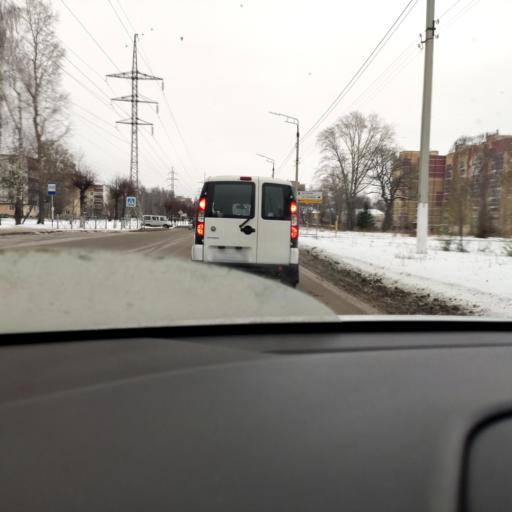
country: RU
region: Tatarstan
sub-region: Zelenodol'skiy Rayon
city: Zelenodolsk
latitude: 55.8532
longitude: 48.5047
